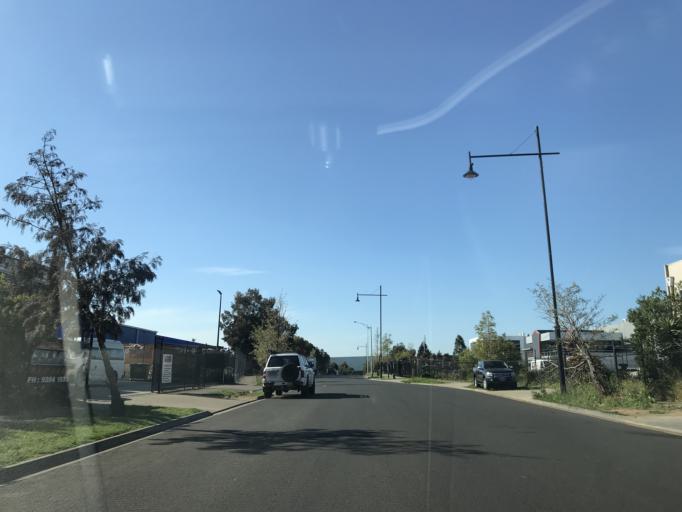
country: AU
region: Victoria
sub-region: Wyndham
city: Truganina
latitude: -37.8063
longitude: 144.7561
